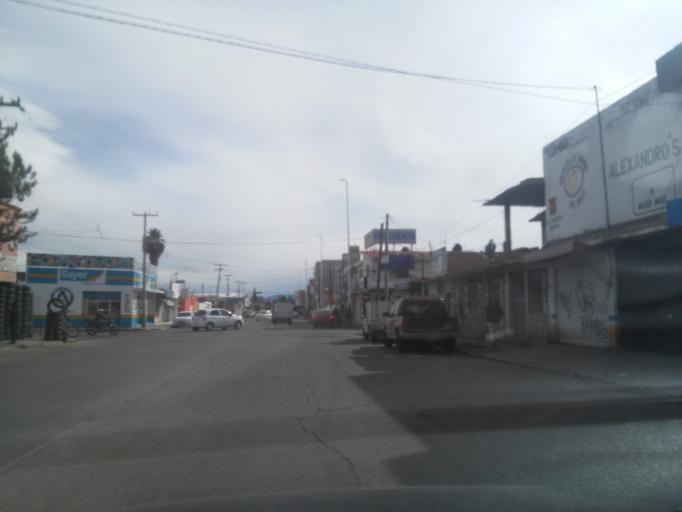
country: MX
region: Durango
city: Victoria de Durango
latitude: 24.0137
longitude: -104.6559
